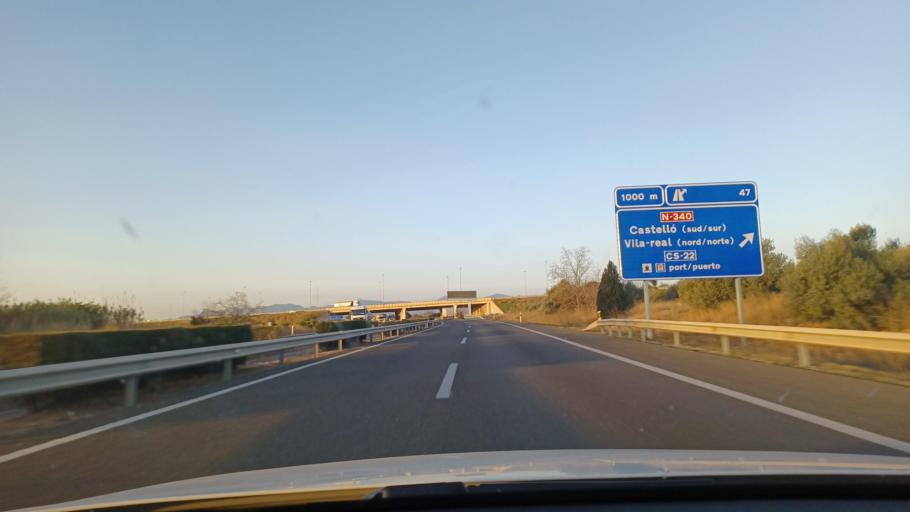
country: ES
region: Valencia
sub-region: Provincia de Castello
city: Castello de la Plana
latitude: 39.9909
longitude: -0.0861
